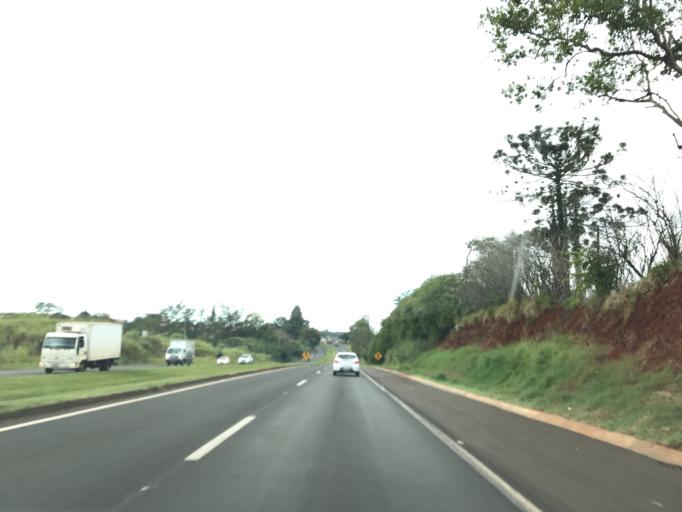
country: BR
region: Parana
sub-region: Cambe
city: Cambe
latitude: -23.2957
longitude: -51.2849
